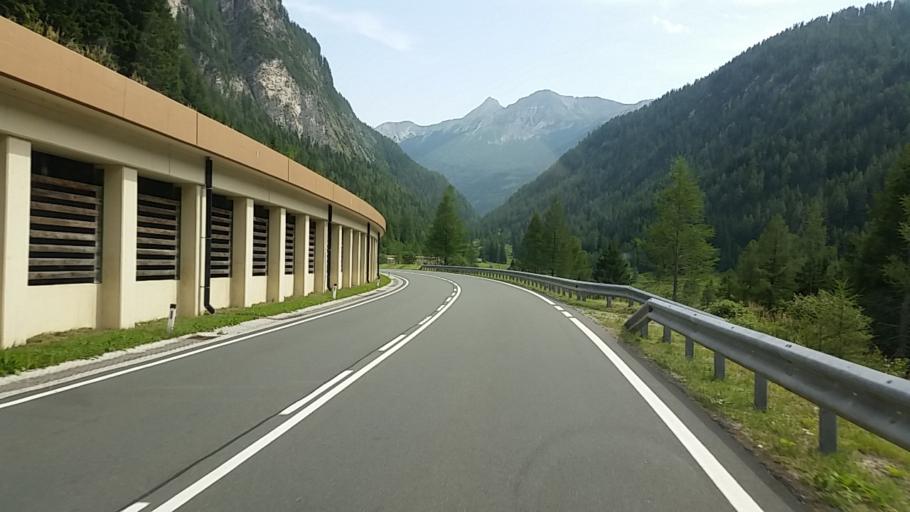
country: AT
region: Salzburg
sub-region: Politischer Bezirk Tamsweg
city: Tweng
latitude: 47.2265
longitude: 13.5799
